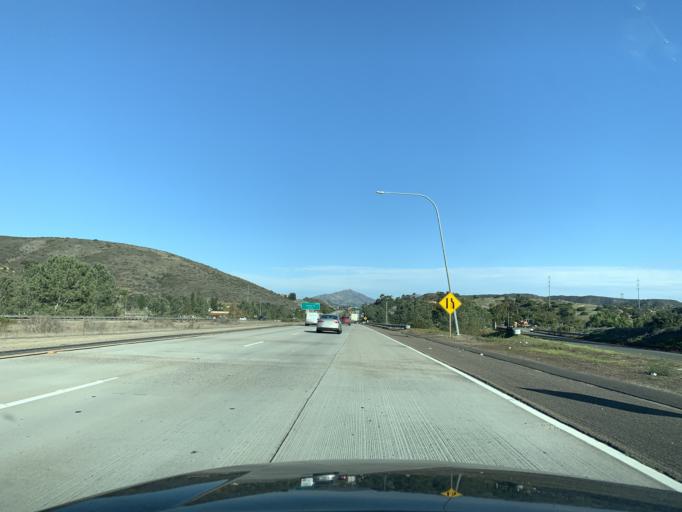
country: US
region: California
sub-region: San Diego County
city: Fairbanks Ranch
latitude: 32.9571
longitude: -117.1173
